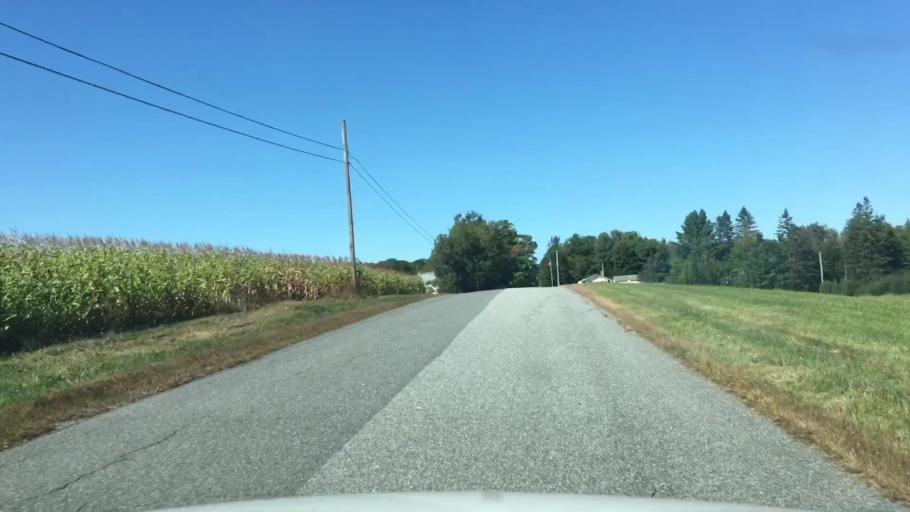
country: US
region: Maine
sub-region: Somerset County
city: Pittsfield
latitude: 44.7875
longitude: -69.4095
